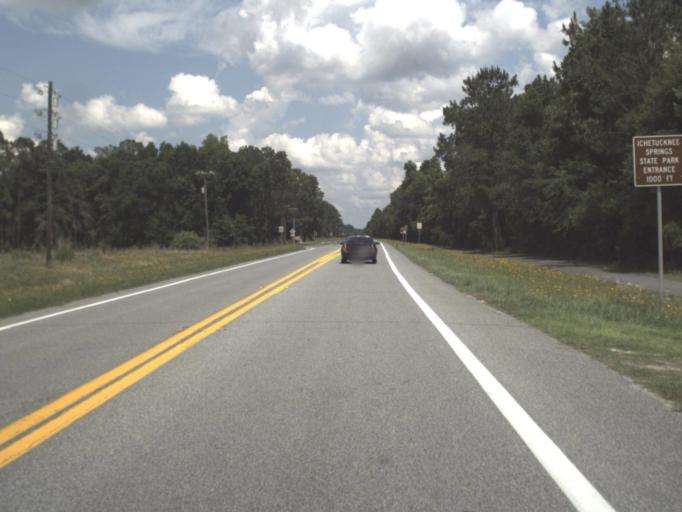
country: US
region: Florida
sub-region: Alachua County
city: High Springs
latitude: 29.9516
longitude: -82.7794
